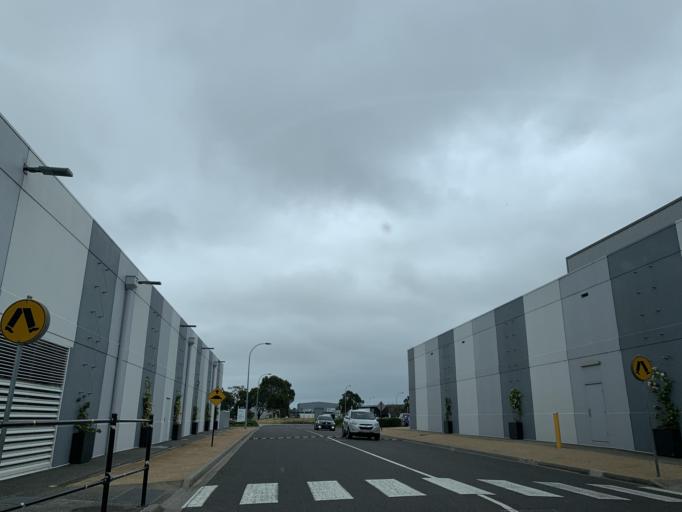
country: AU
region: Victoria
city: Heatherton
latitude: -37.9703
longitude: 145.0907
